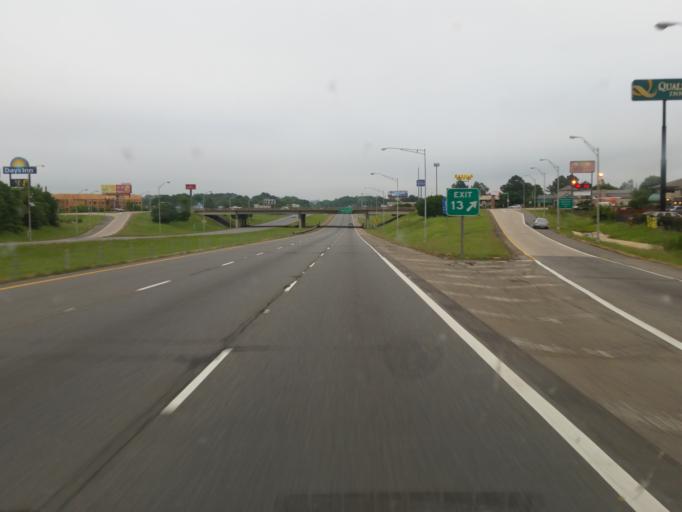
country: US
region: Louisiana
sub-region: Caddo Parish
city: Shreveport
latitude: 32.4605
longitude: -93.8303
